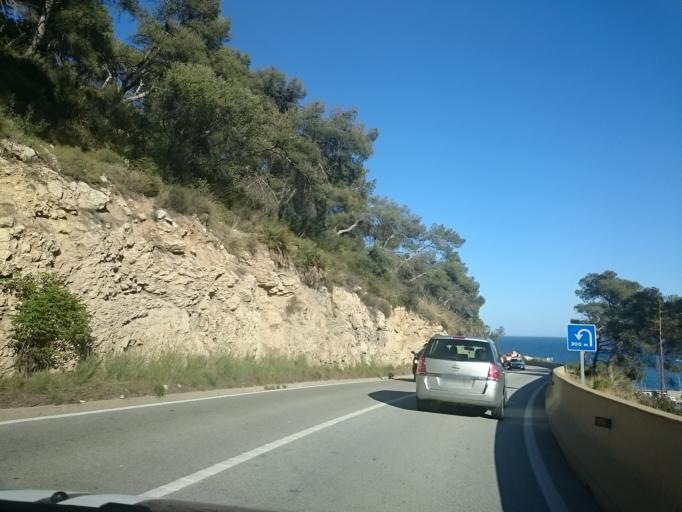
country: ES
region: Catalonia
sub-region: Provincia de Barcelona
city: Castelldefels
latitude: 41.2533
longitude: 1.8976
